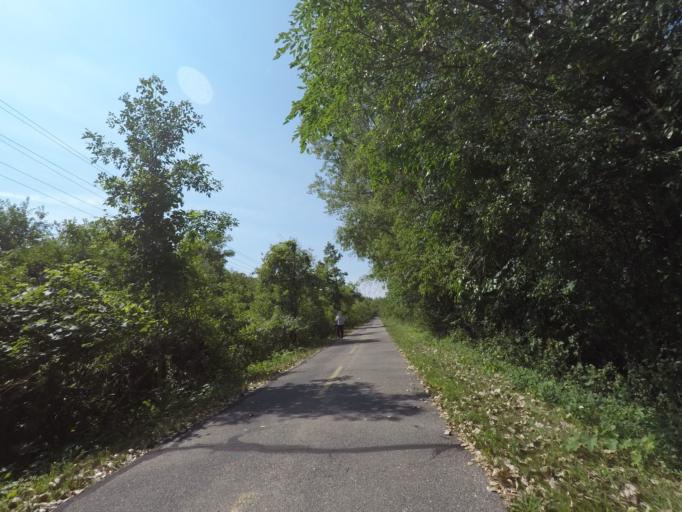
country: US
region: Wisconsin
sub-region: Jefferson County
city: Fort Atkinson
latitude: 42.9081
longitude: -88.8552
